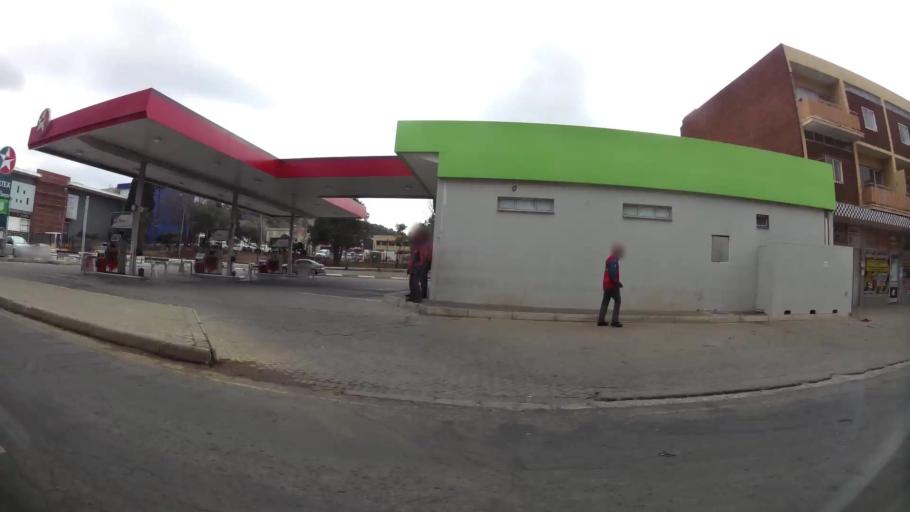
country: ZA
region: Orange Free State
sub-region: Mangaung Metropolitan Municipality
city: Bloemfontein
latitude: -29.1127
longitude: 26.2182
